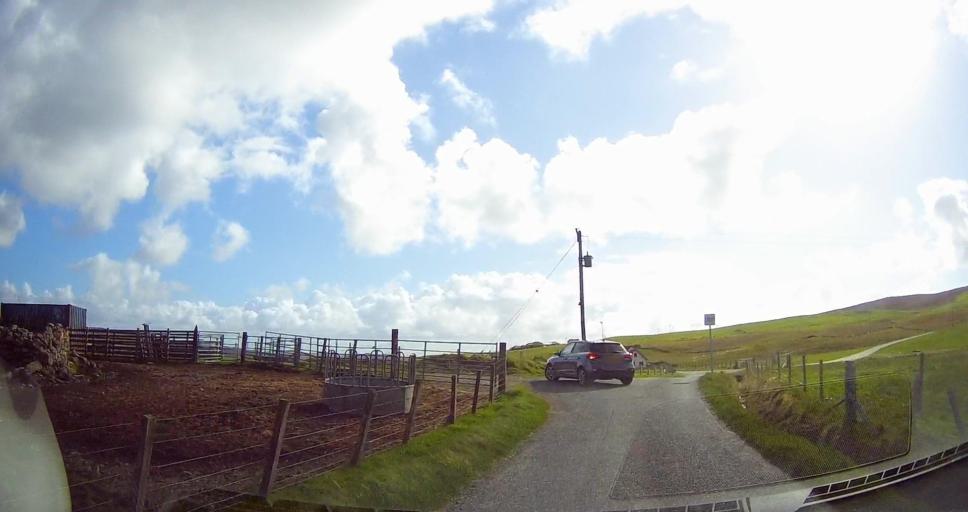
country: GB
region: Scotland
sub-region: Shetland Islands
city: Lerwick
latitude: 60.3577
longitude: -1.3863
